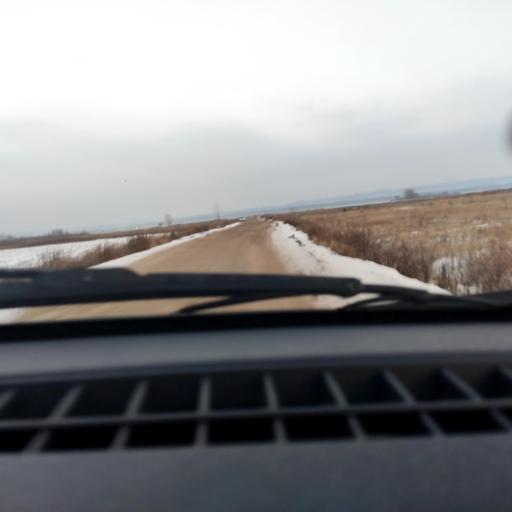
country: RU
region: Bashkortostan
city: Mikhaylovka
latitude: 54.8091
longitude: 55.9544
